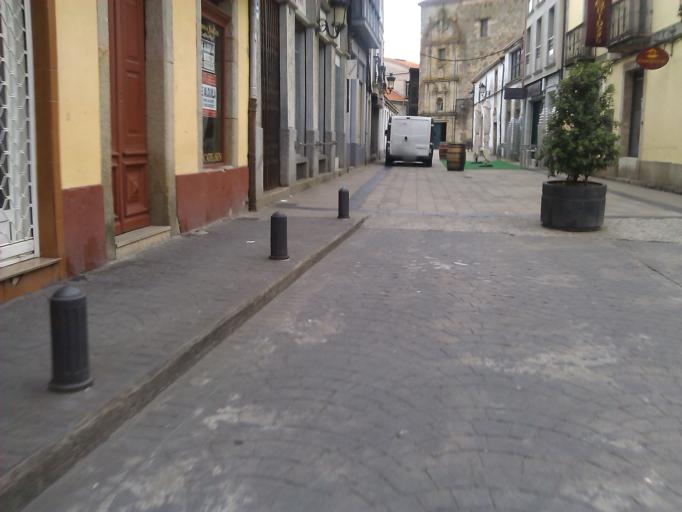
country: ES
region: Galicia
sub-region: Provincia da Coruna
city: Melide
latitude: 42.9149
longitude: -8.0158
